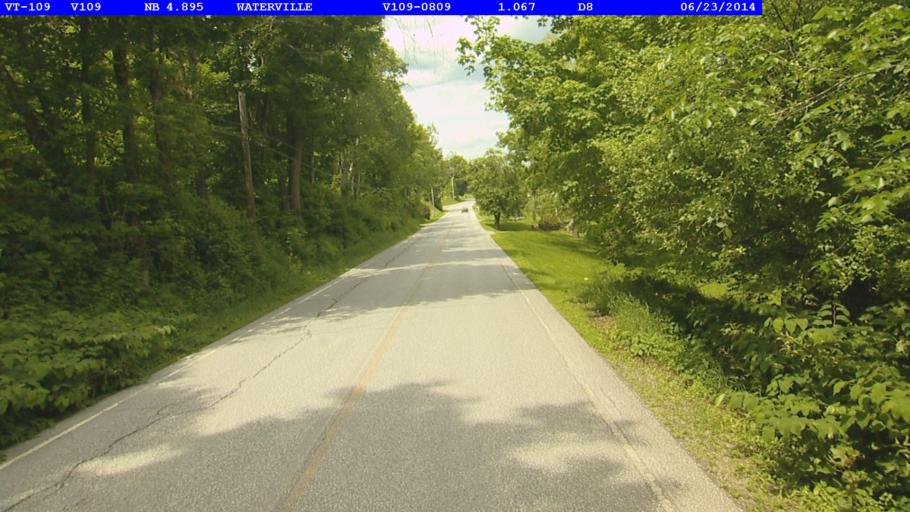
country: US
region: Vermont
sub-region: Lamoille County
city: Johnson
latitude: 44.6969
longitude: -72.7653
